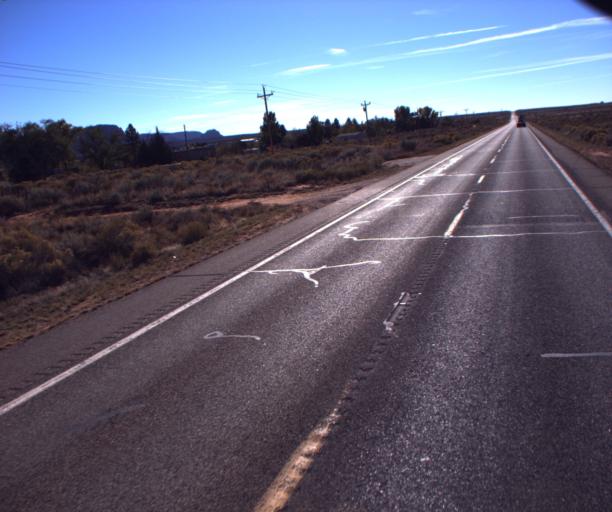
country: US
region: Arizona
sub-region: Mohave County
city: Colorado City
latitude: 36.9304
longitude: -112.9432
